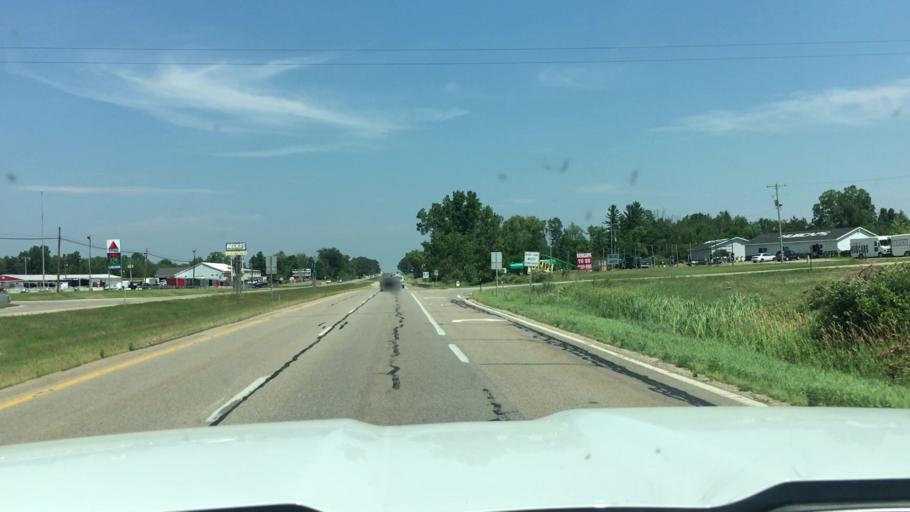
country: US
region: Michigan
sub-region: Clinton County
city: Saint Johns
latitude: 43.0958
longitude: -84.5634
